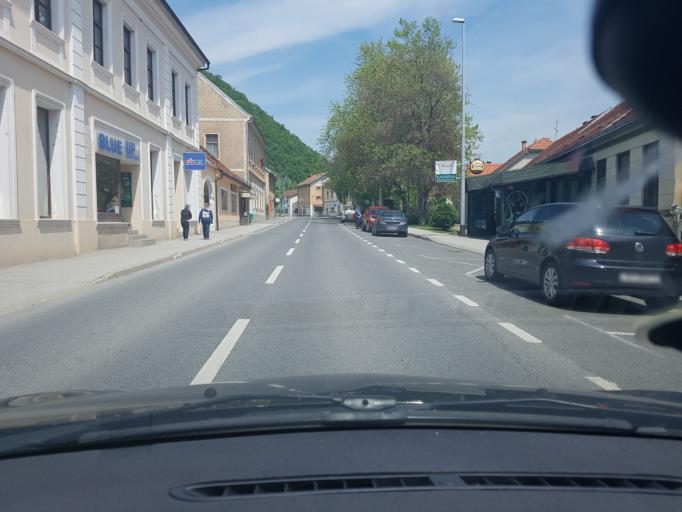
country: HR
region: Krapinsko-Zagorska
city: Pregrada
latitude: 46.1636
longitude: 15.7502
